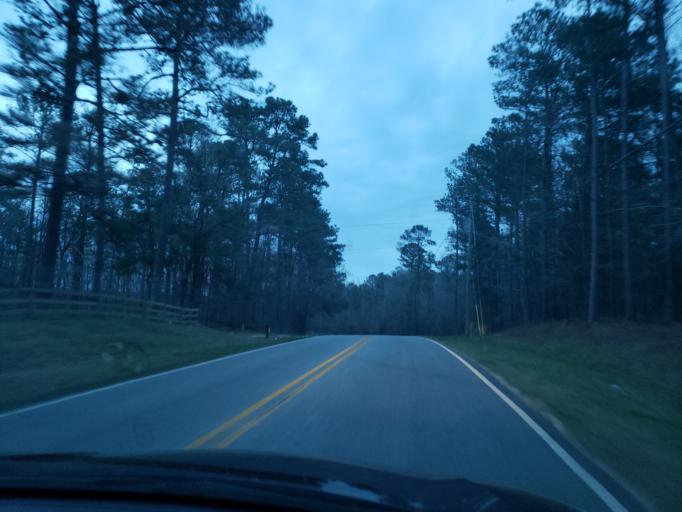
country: US
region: Alabama
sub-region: Lee County
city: Auburn
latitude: 32.6491
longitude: -85.4536
